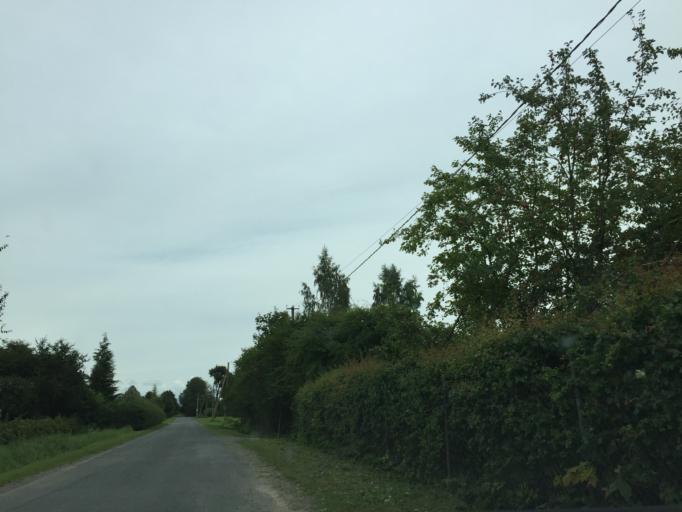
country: LV
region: Ogre
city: Ogre
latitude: 56.7680
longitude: 24.6505
